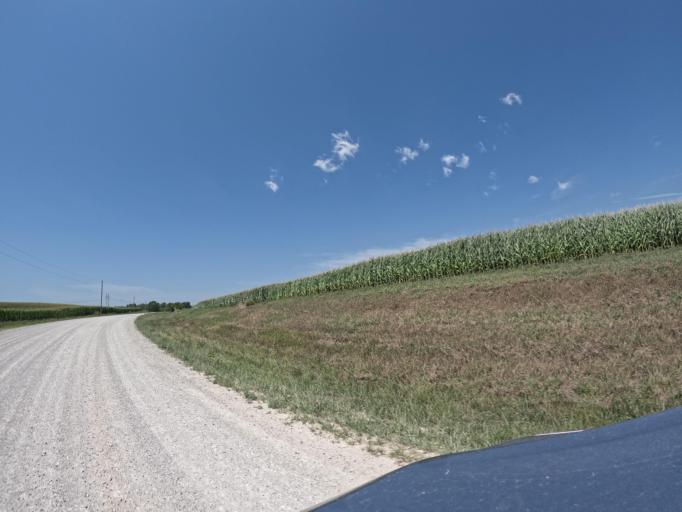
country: US
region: Iowa
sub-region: Henry County
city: Mount Pleasant
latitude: 40.9379
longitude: -91.6346
